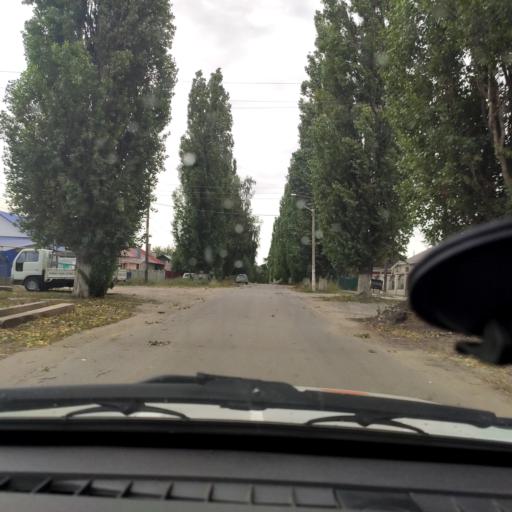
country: RU
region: Voronezj
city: Strelitsa
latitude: 51.6072
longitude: 38.9066
